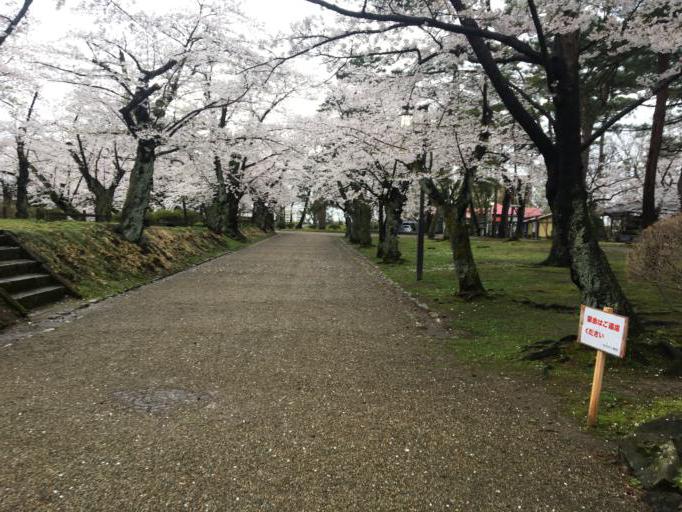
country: JP
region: Akita
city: Akita
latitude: 39.7221
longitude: 140.1243
